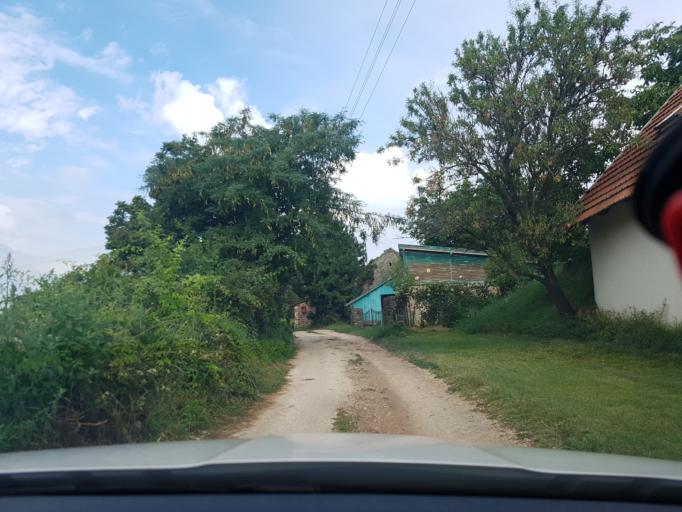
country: HU
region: Veszprem
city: Balatonalmadi
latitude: 46.9935
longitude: 17.9793
